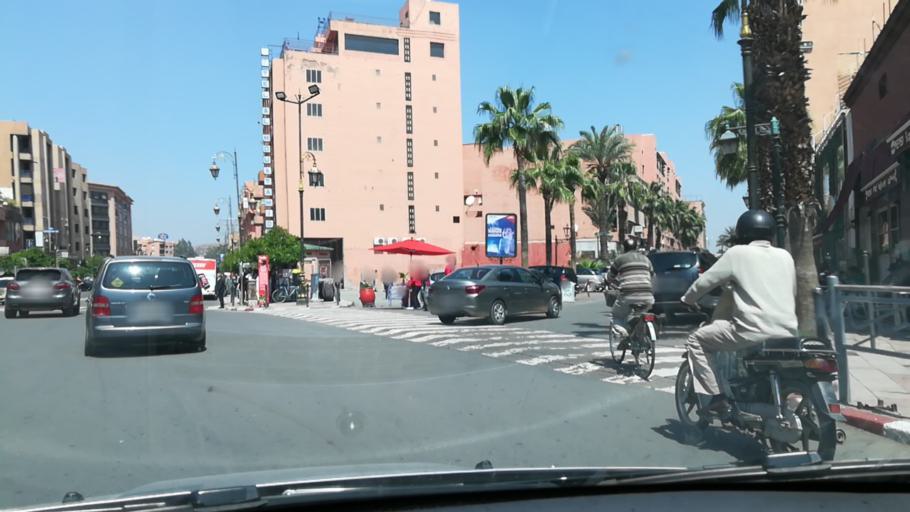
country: MA
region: Marrakech-Tensift-Al Haouz
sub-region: Marrakech
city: Marrakesh
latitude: 31.6361
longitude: -8.0145
